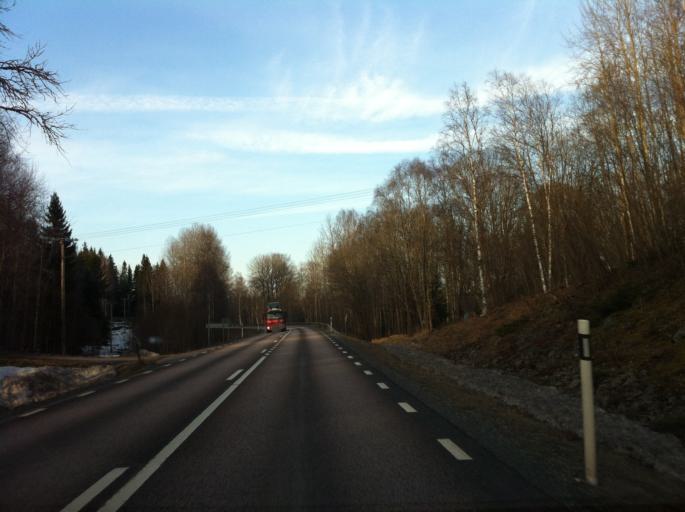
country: SE
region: Vaermland
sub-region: Filipstads Kommun
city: Lesjofors
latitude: 59.8603
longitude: 14.2668
